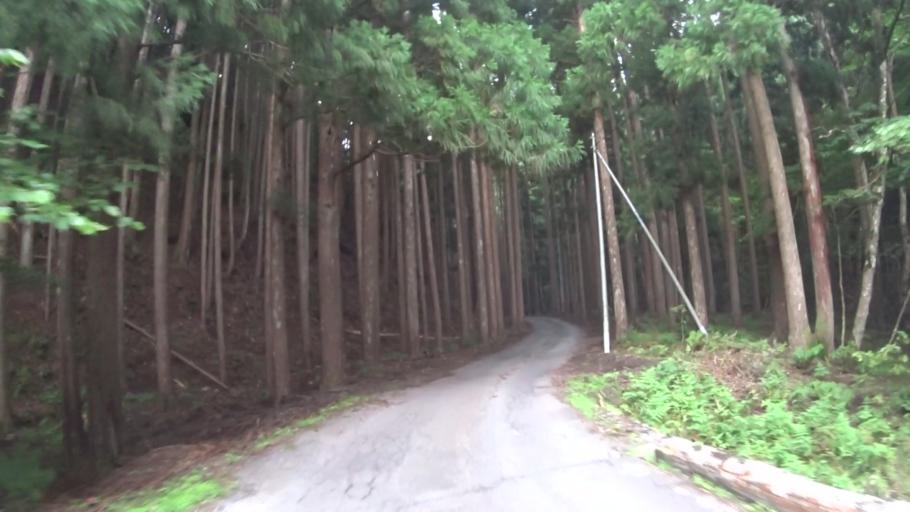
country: JP
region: Shiga Prefecture
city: Kitahama
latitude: 35.2638
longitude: 135.7817
